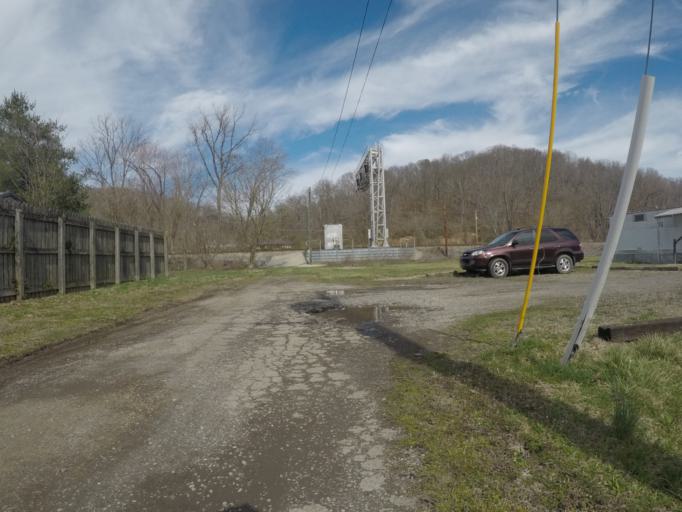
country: US
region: West Virginia
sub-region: Cabell County
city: Pea Ridge
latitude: 38.4183
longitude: -82.3532
